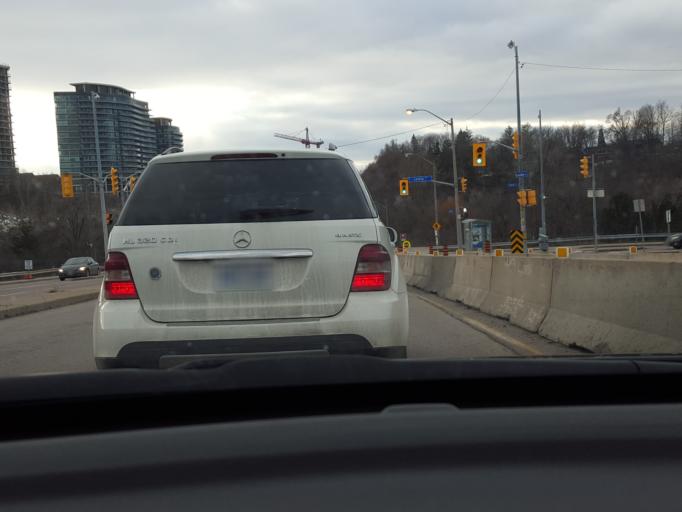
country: CA
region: Ontario
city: Toronto
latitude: 43.7174
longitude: -79.3492
